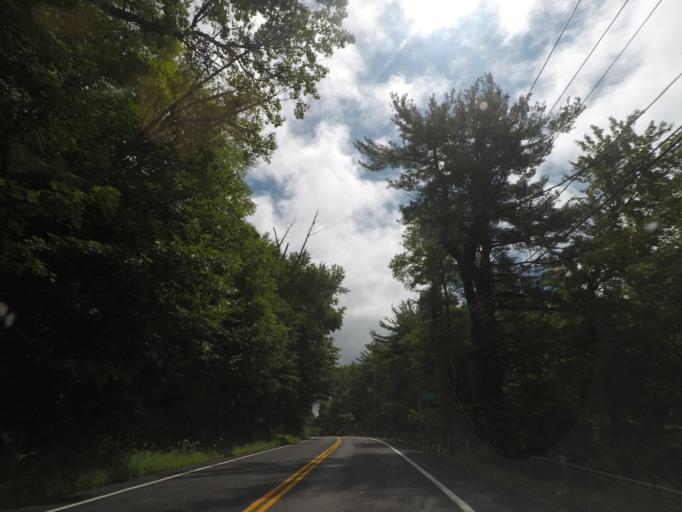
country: US
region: New York
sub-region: Rensselaer County
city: Averill Park
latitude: 42.5981
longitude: -73.5148
